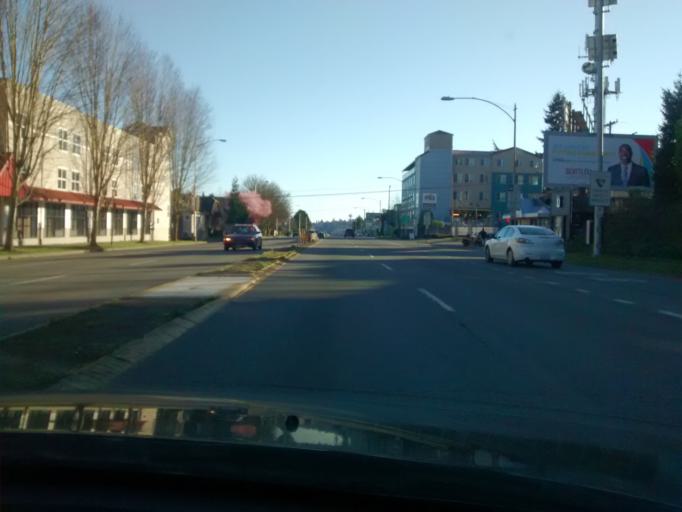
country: US
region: Washington
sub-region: King County
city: Seattle
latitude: 47.6649
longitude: -122.3473
